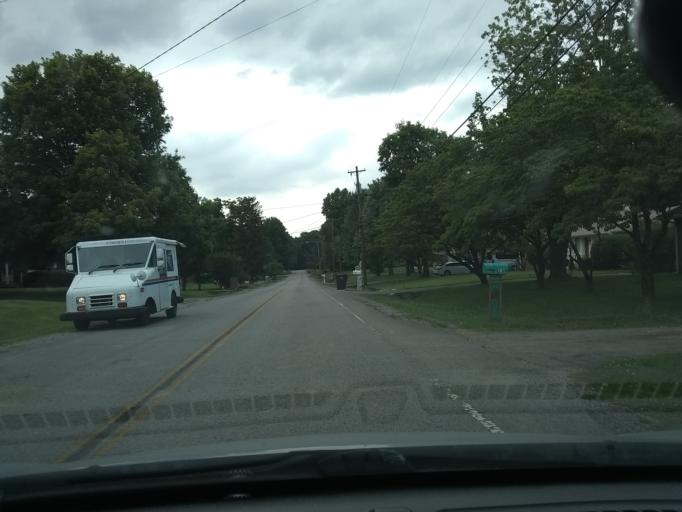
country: US
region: Tennessee
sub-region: Davidson County
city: Oak Hill
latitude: 36.1203
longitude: -86.7064
